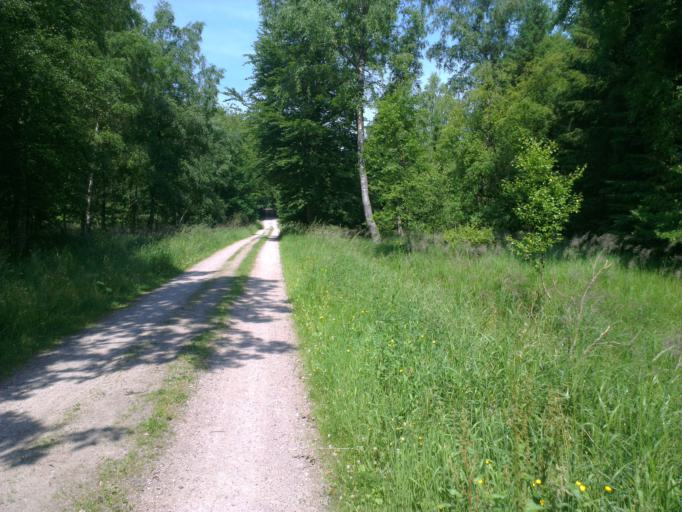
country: DK
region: Capital Region
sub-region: Allerod Kommune
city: Lillerod
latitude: 55.9180
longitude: 12.3514
